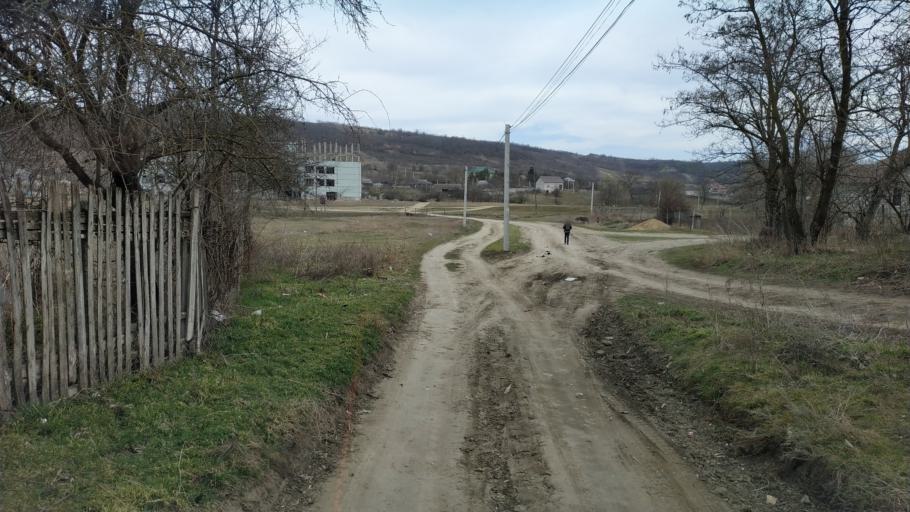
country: MD
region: Hincesti
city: Dancu
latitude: 46.9220
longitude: 28.2690
